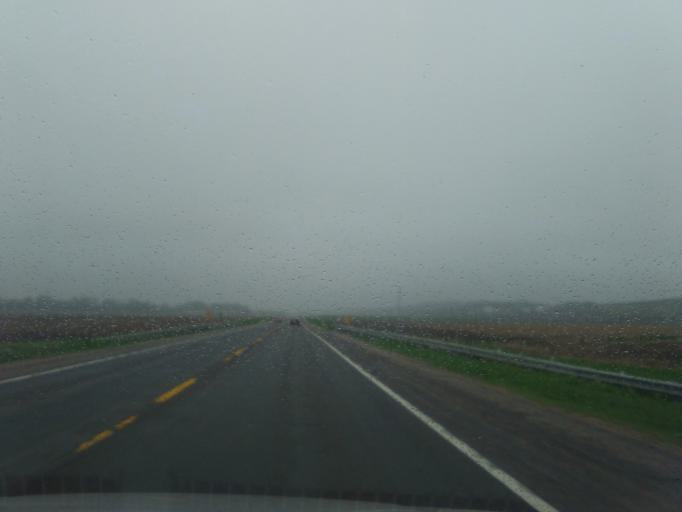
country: US
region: Nebraska
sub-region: Cuming County
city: Wisner
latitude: 41.9628
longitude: -96.8797
